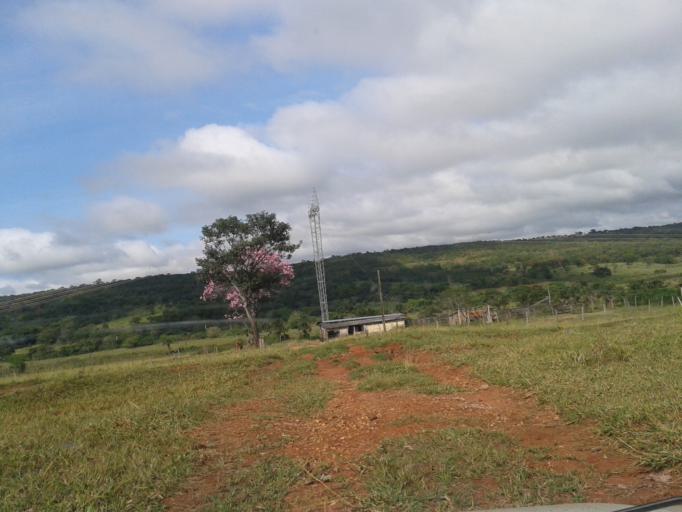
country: BR
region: Minas Gerais
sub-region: Campina Verde
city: Campina Verde
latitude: -19.4292
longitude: -49.6580
